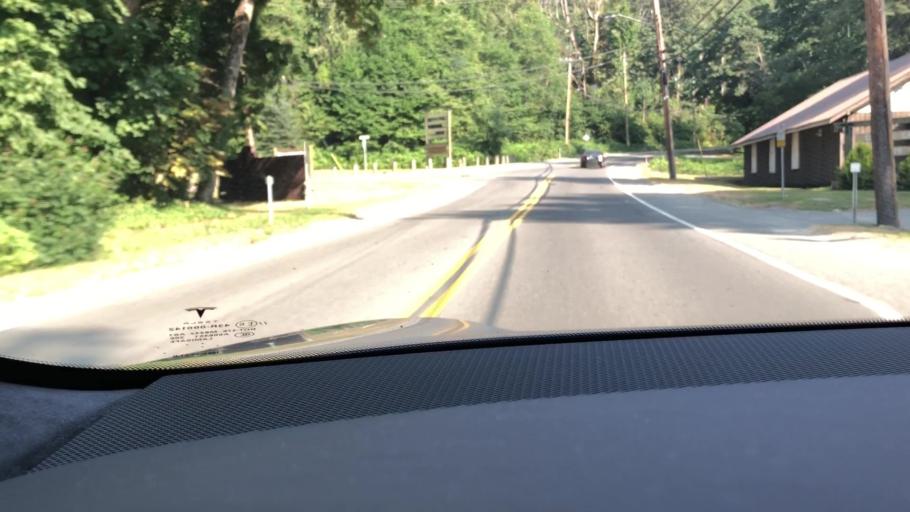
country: CA
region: British Columbia
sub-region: Fraser Valley Regional District
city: Chilliwack
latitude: 49.0780
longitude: -121.9792
